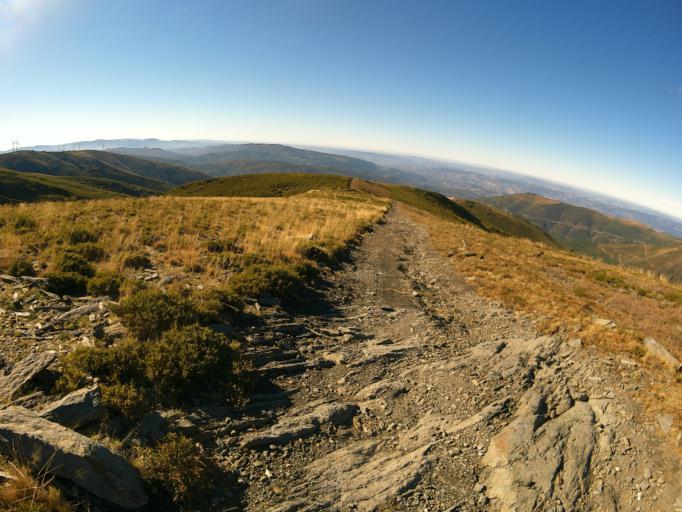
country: PT
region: Vila Real
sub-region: Mesao Frio
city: Mesao Frio
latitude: 41.2549
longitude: -7.9021
